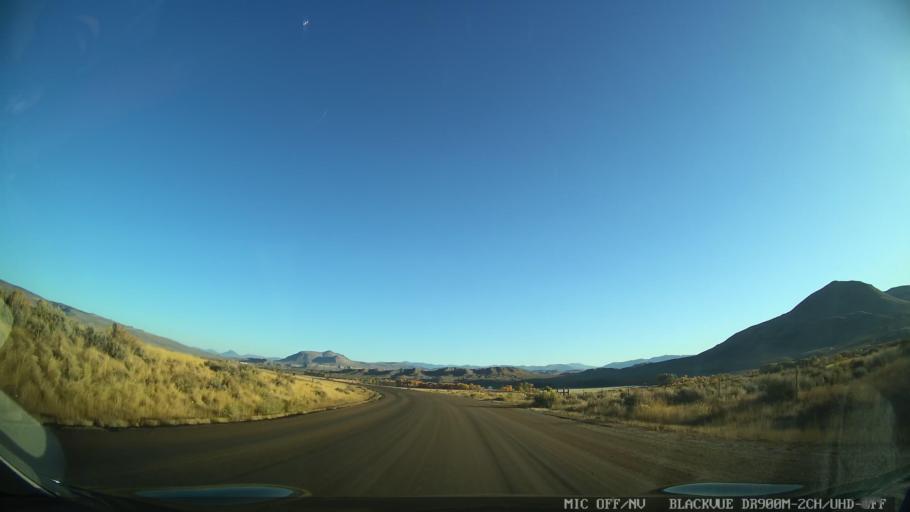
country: US
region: Colorado
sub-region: Grand County
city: Kremmling
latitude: 40.0184
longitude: -106.3886
